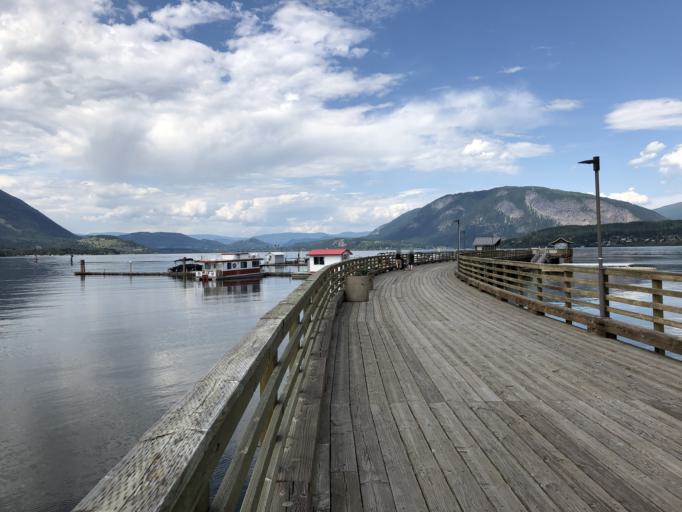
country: CA
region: British Columbia
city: Salmon Arm
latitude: 50.7082
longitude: -119.2842
